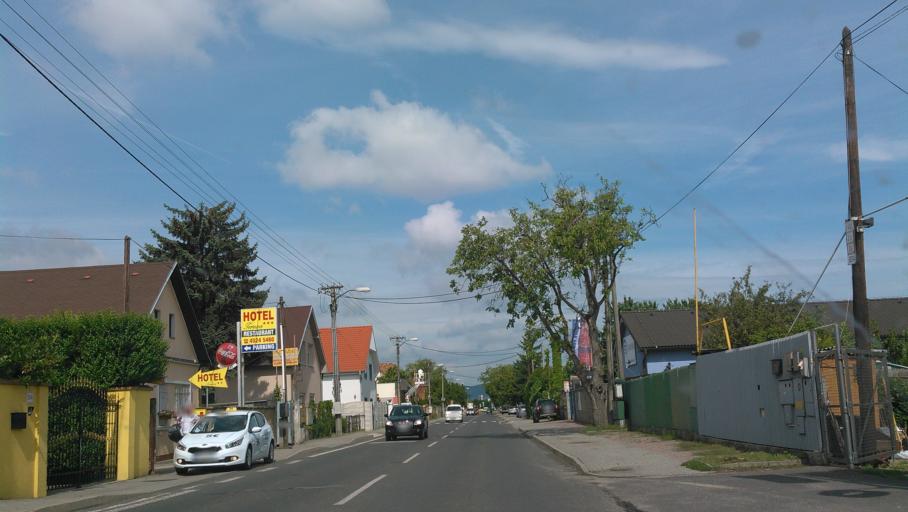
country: SK
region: Bratislavsky
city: Bratislava
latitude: 48.1527
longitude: 17.1986
